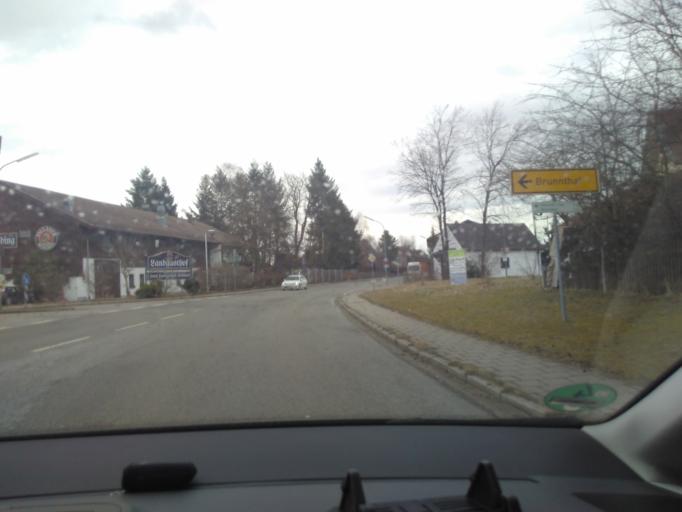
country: DE
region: Bavaria
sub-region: Upper Bavaria
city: Brunnthal
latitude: 47.9829
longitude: 11.7004
